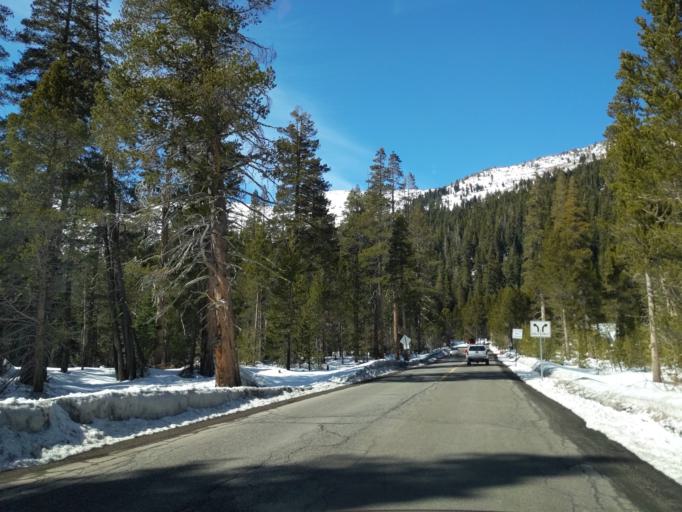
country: US
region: California
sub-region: El Dorado County
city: South Lake Tahoe
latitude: 38.8177
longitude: -120.0743
